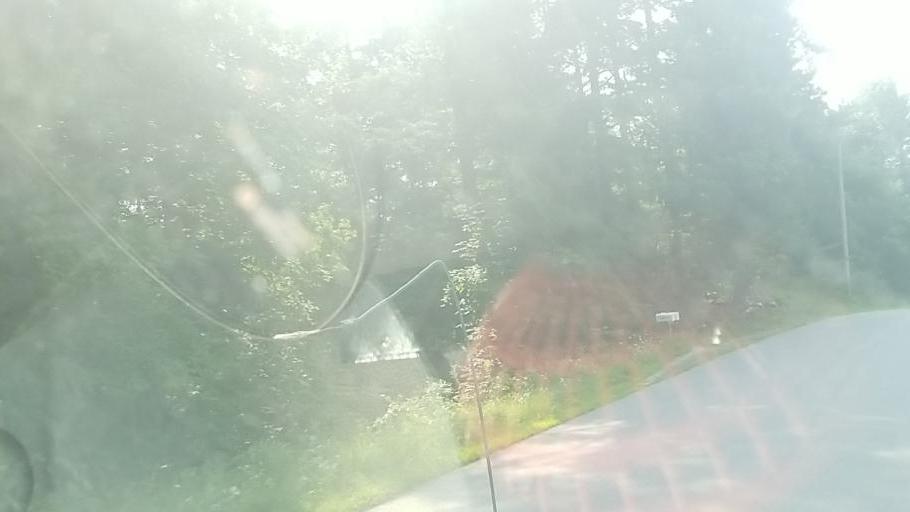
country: US
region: New York
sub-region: Montgomery County
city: Fonda
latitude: 42.9264
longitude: -74.4466
